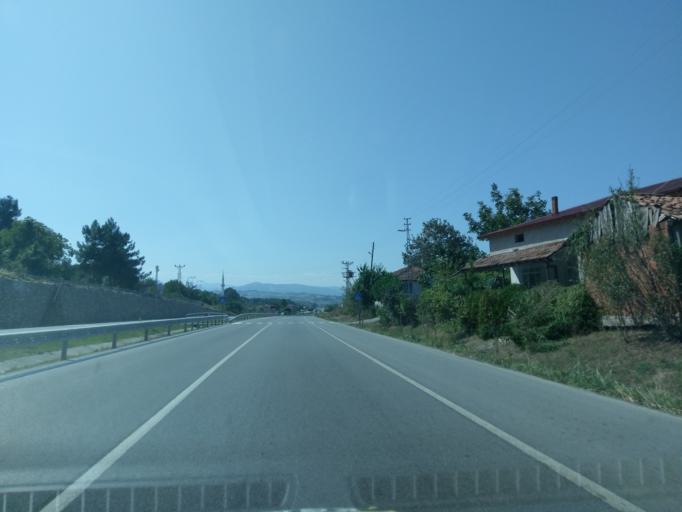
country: TR
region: Samsun
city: Alacam
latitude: 41.6084
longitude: 35.6882
